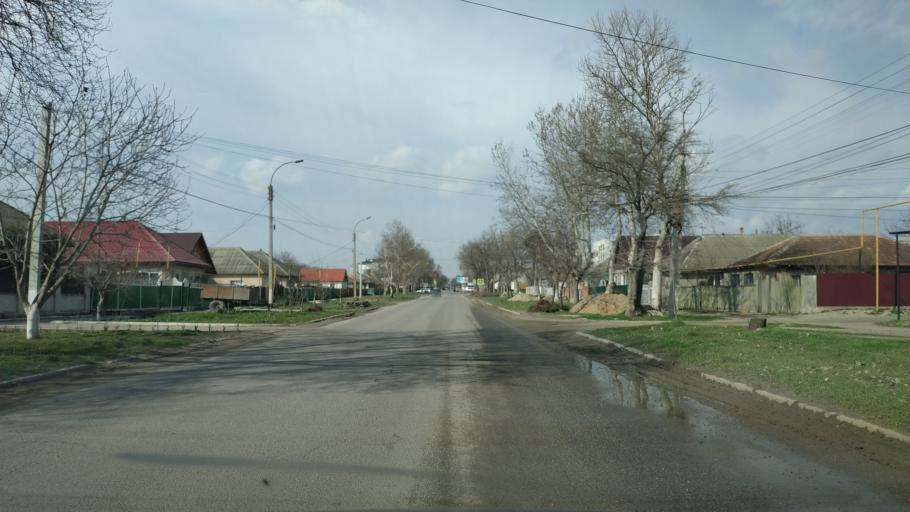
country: MD
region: Gagauzia
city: Vulcanesti
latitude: 45.6791
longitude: 28.4099
